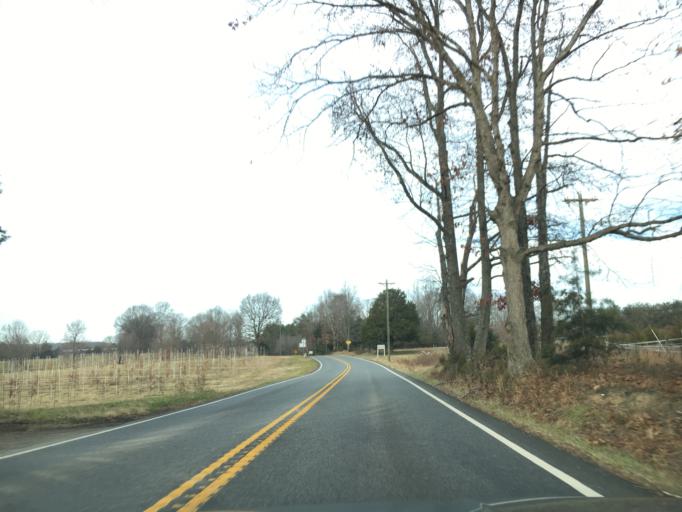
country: US
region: Virginia
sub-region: Goochland County
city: Goochland
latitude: 37.8259
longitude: -77.8916
